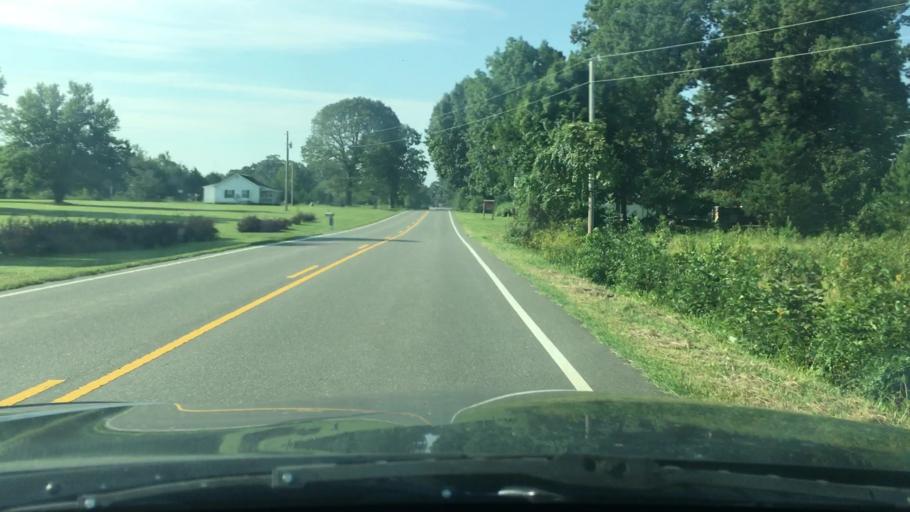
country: US
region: North Carolina
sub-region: Caswell County
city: Yanceyville
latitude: 36.2750
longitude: -79.3481
